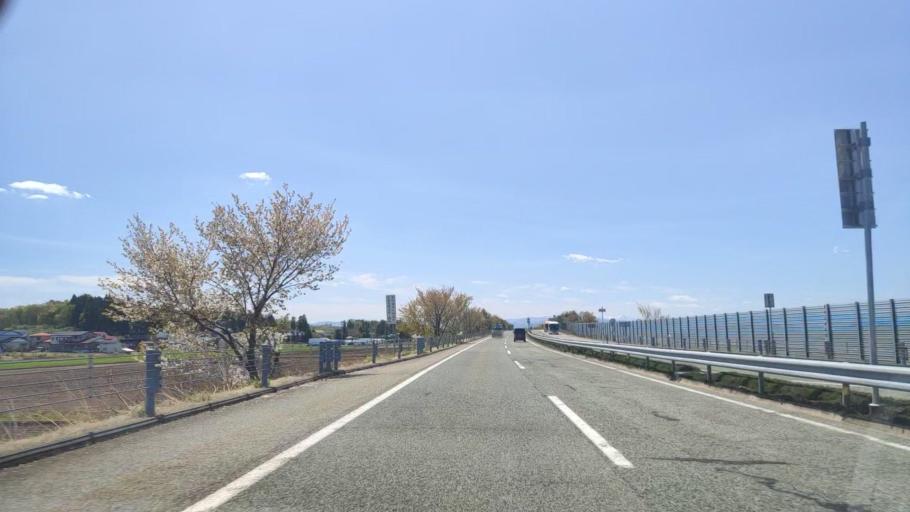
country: JP
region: Akita
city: Yokotemachi
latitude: 39.3192
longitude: 140.5153
